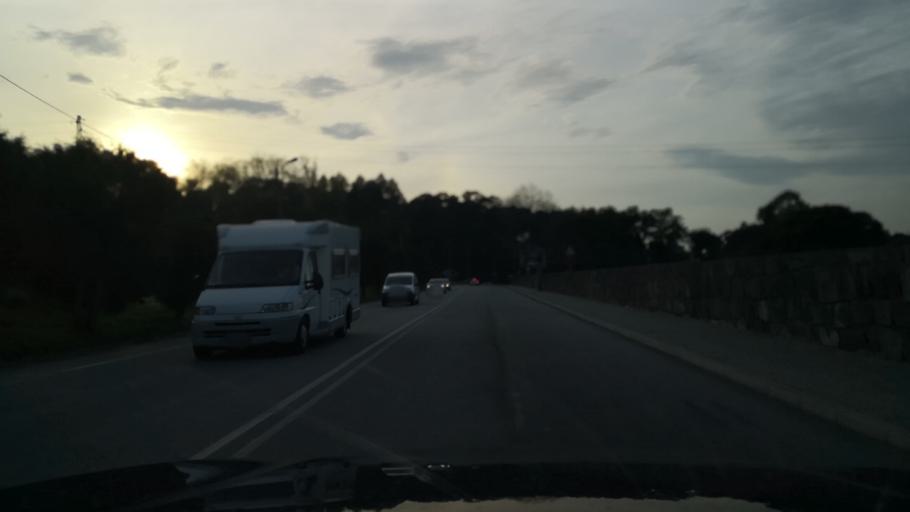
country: PT
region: Porto
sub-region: Maia
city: Leca do Bailio
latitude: 41.2078
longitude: -8.6230
